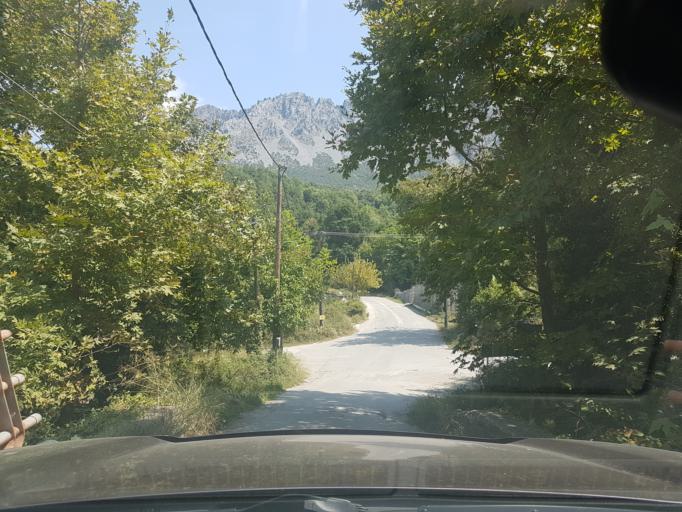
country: GR
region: Central Greece
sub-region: Nomos Evvoias
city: Kymi
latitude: 38.6259
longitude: 23.9487
